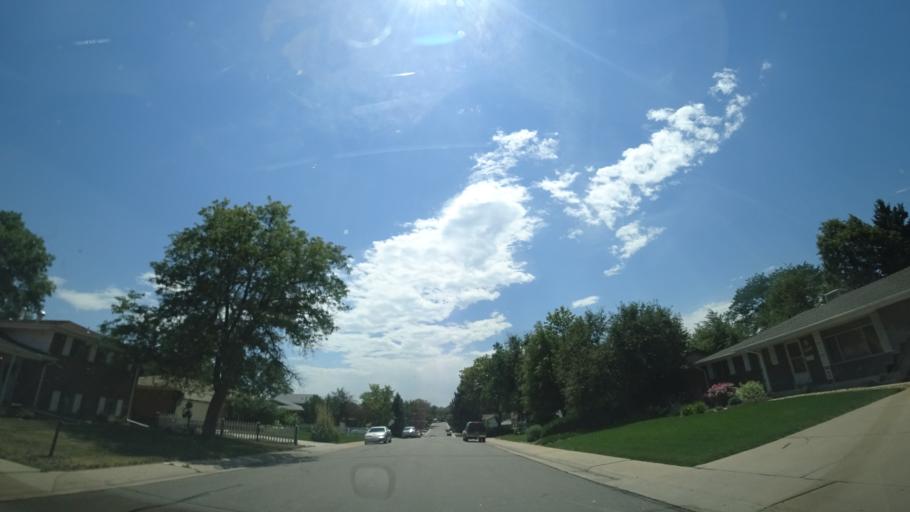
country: US
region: Colorado
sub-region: Jefferson County
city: Lakewood
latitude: 39.6933
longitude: -105.0934
